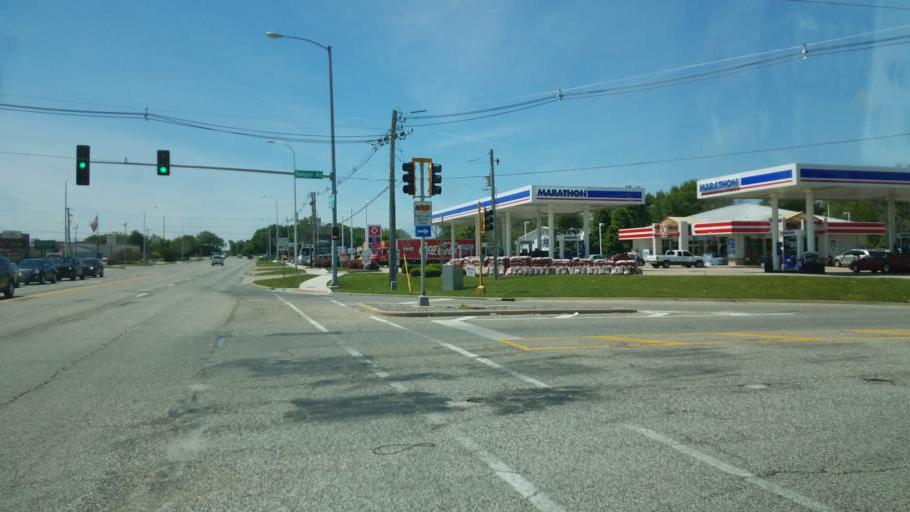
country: US
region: Illinois
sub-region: Champaign County
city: Urbana
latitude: 40.1305
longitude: -88.1978
